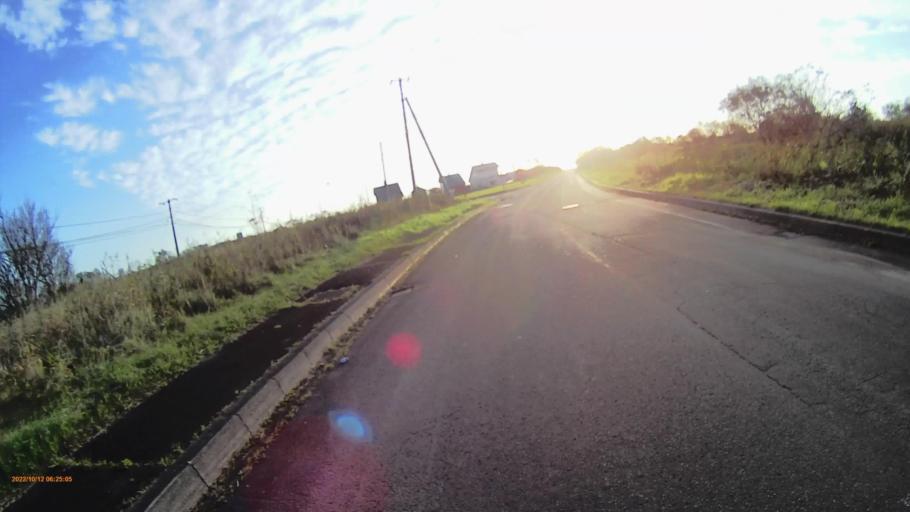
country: JP
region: Hokkaido
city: Kushiro
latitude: 42.8897
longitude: 143.9369
